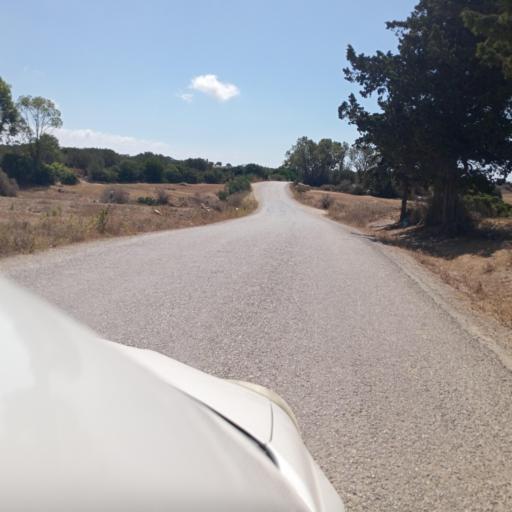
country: TN
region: Nabul
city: Qulaybiyah
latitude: 36.8628
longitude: 11.0382
